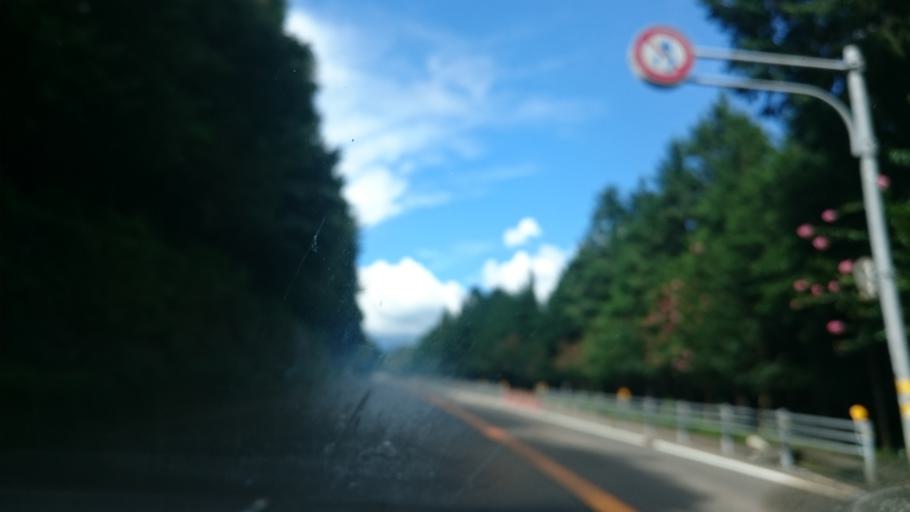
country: JP
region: Gifu
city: Nakatsugawa
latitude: 35.5713
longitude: 137.4558
